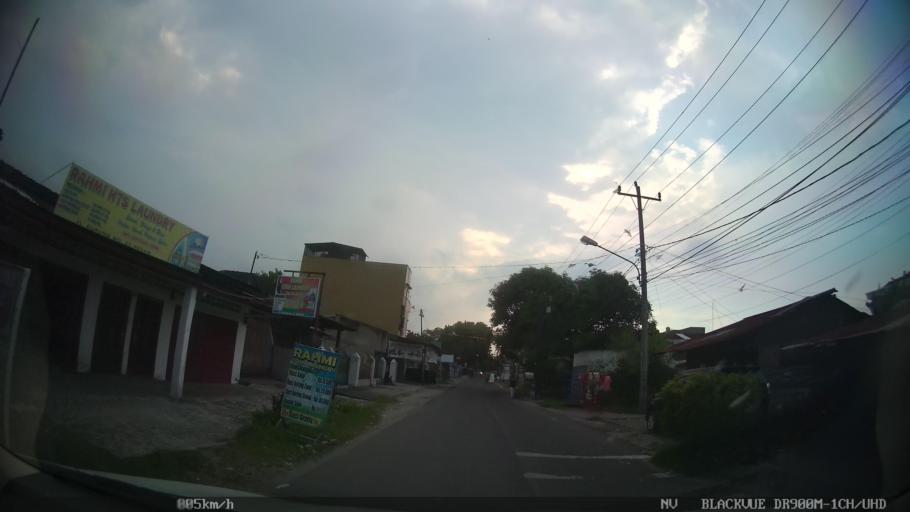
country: ID
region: North Sumatra
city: Medan
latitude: 3.6094
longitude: 98.6963
